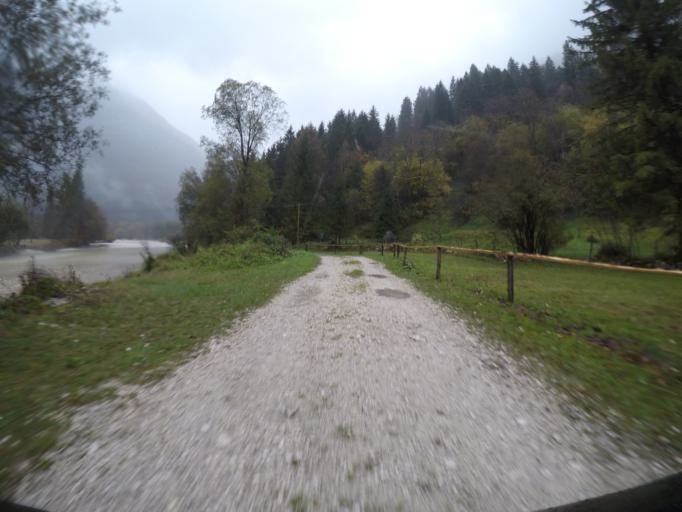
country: SI
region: Bovec
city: Bovec
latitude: 46.3321
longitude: 13.6386
